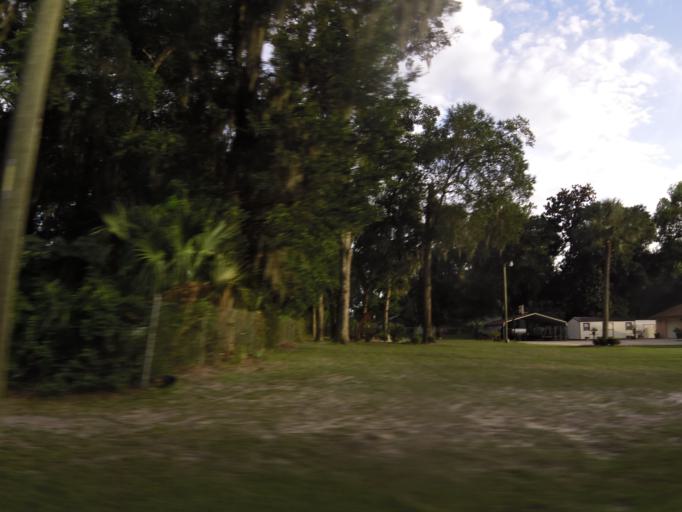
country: US
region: Florida
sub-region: Duval County
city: Jacksonville
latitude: 30.4151
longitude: -81.7001
